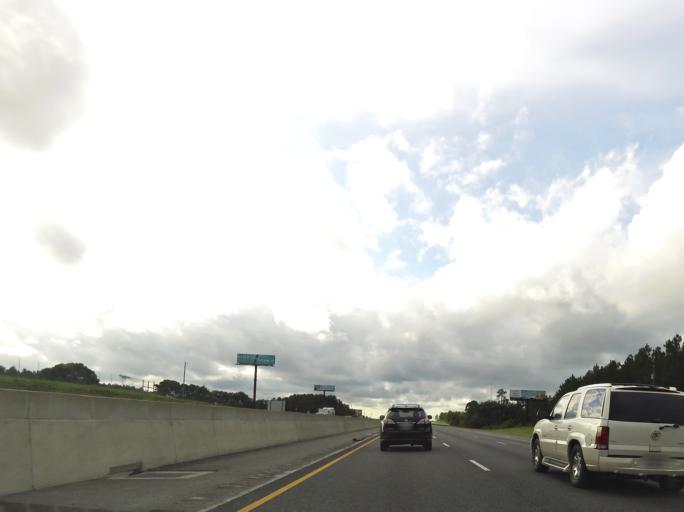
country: US
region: Georgia
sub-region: Turner County
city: Ashburn
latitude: 31.7278
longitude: -83.6454
